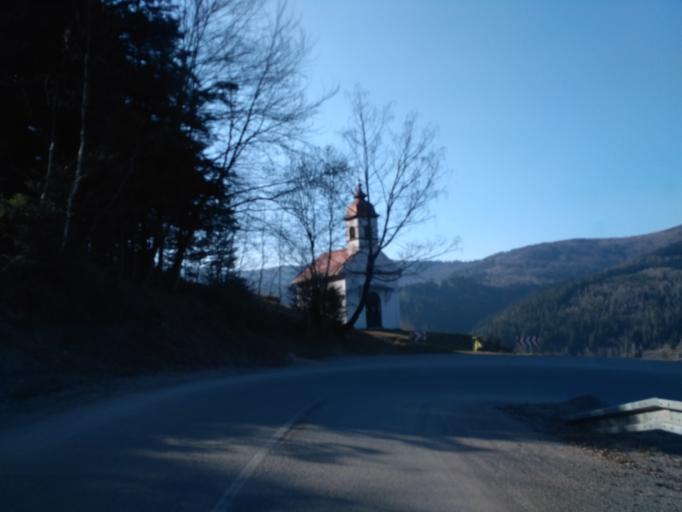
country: SK
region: Kosicky
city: Medzev
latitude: 48.7237
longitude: 20.7335
